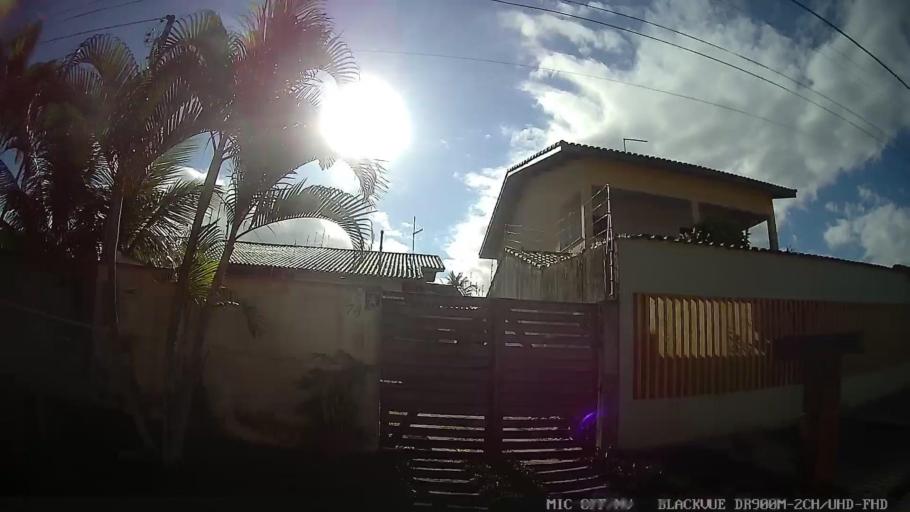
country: BR
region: Sao Paulo
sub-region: Itanhaem
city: Itanhaem
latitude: -24.2156
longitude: -46.8505
